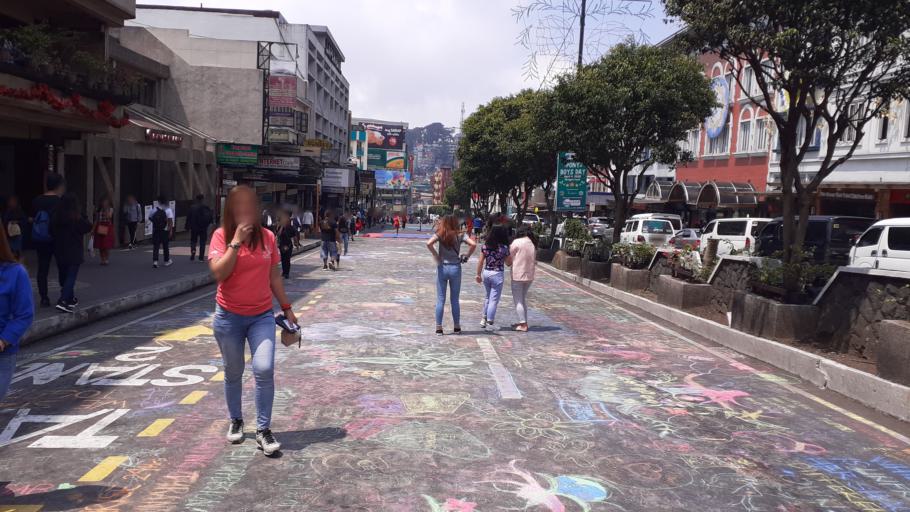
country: PH
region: Cordillera
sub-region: Baguio City
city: Baguio
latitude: 16.4118
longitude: 120.5983
